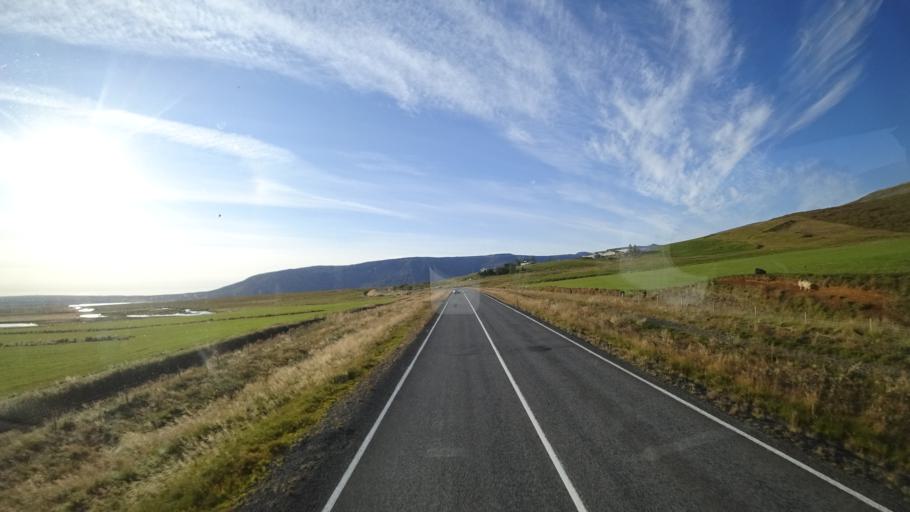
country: IS
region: South
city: Selfoss
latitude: 64.2237
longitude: -20.6193
